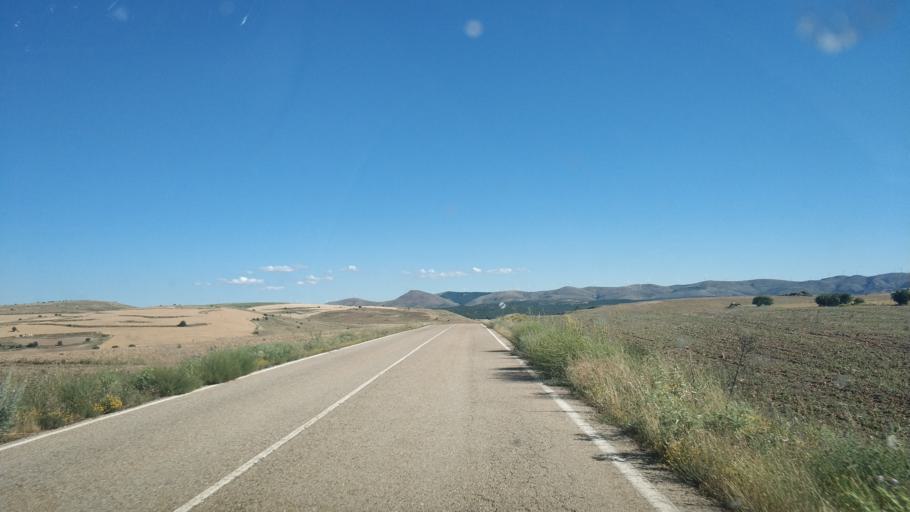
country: ES
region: Castille and Leon
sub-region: Provincia de Soria
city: Montejo de Tiermes
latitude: 41.3815
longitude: -3.1932
